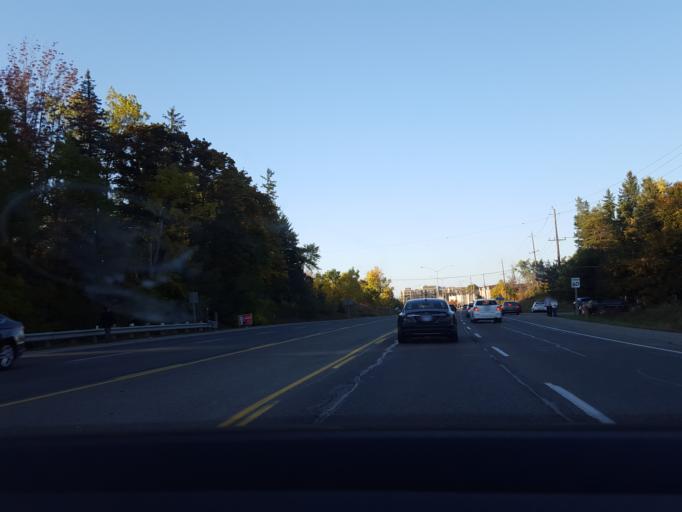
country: CA
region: Ontario
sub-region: York
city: Richmond Hill
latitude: 43.9362
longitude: -79.4536
